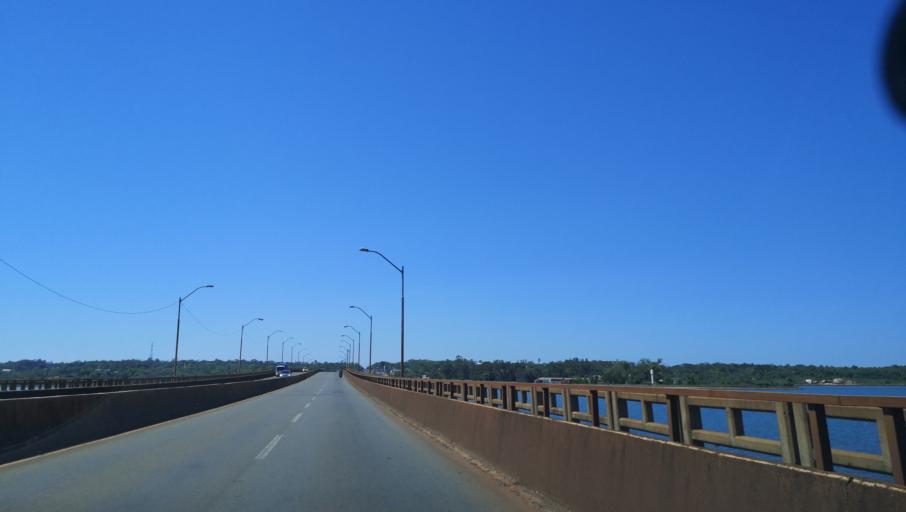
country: PY
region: Itapua
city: Encarnacion
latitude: -27.2979
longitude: -55.9039
